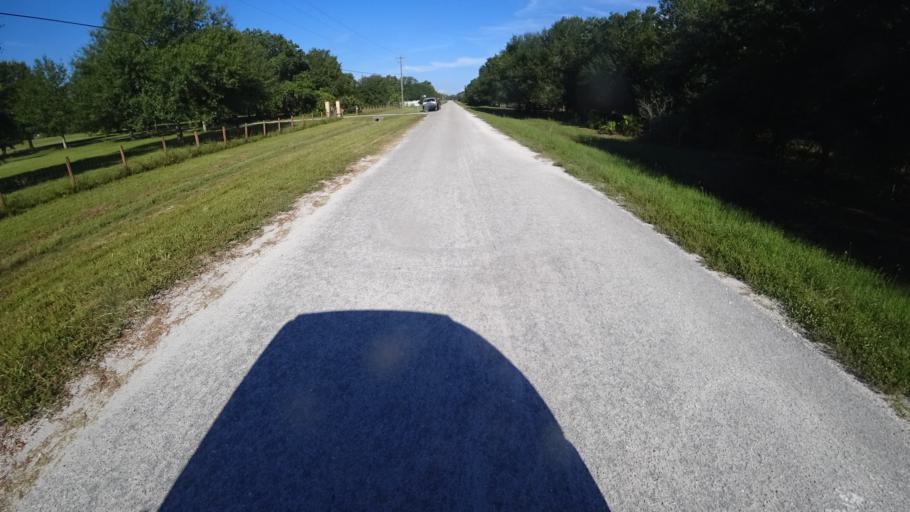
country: US
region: Florida
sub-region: Sarasota County
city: Lake Sarasota
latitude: 27.4119
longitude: -82.2523
